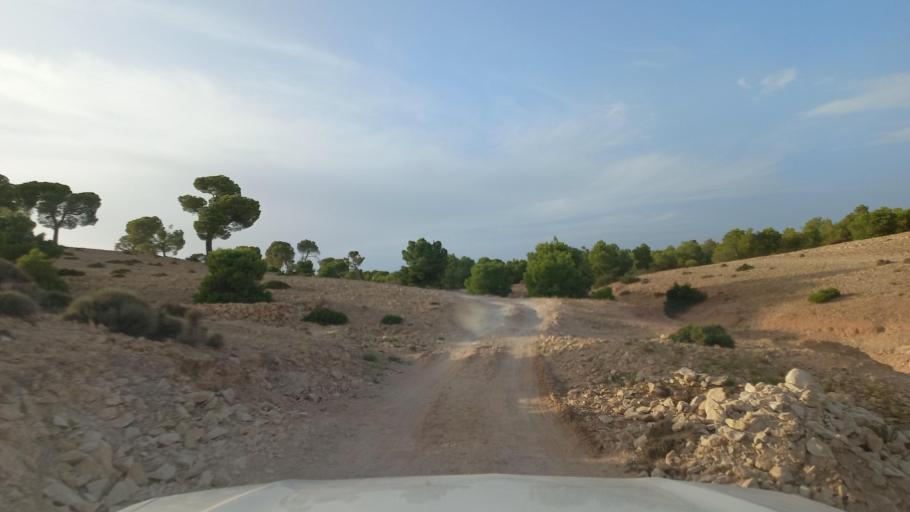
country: TN
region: Al Qasrayn
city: Sbiba
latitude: 35.4112
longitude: 8.8975
